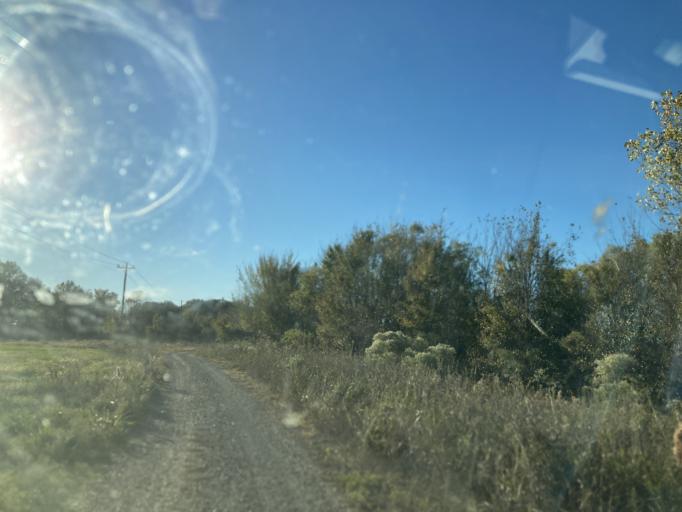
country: US
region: Mississippi
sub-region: Yazoo County
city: Yazoo City
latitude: 32.8922
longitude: -90.4287
